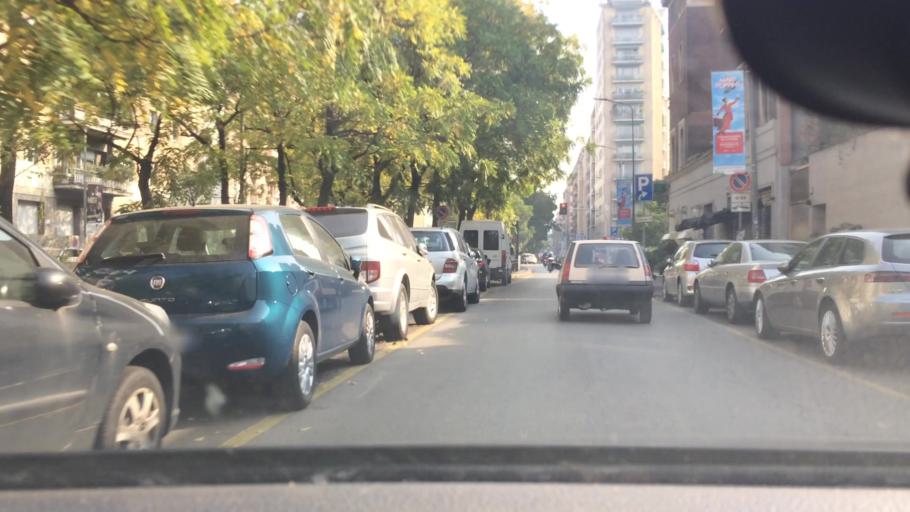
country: IT
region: Lombardy
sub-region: Citta metropolitana di Milano
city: Milano
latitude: 45.4751
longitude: 9.2100
